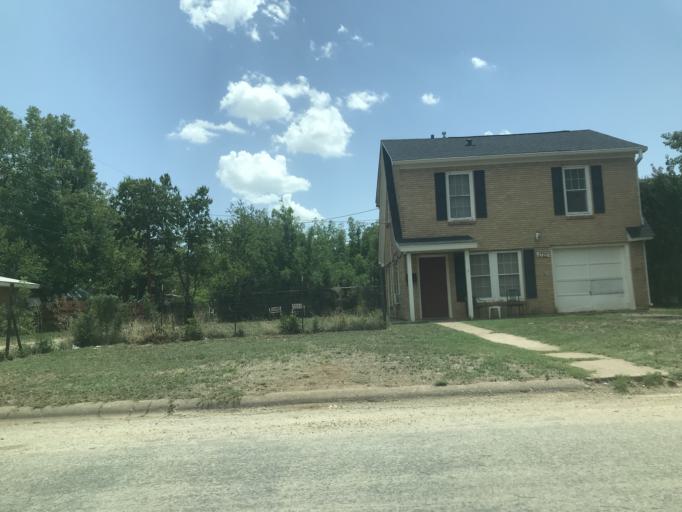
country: US
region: Texas
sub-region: Taylor County
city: Abilene
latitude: 32.4680
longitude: -99.7145
